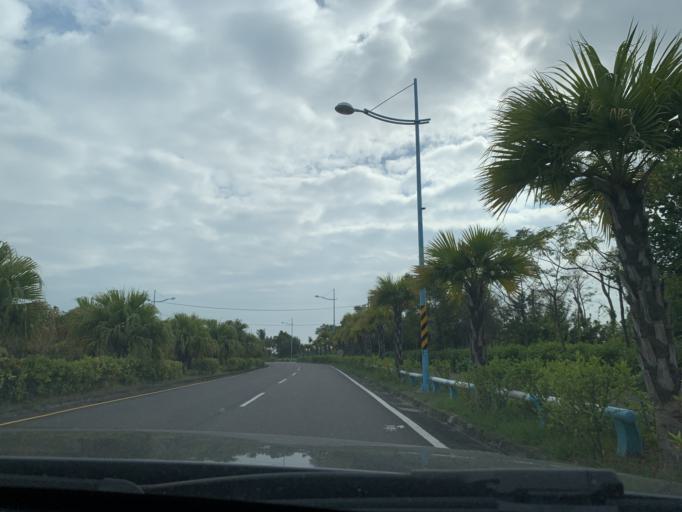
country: TW
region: Taiwan
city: Fengshan
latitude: 22.4461
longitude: 120.4877
